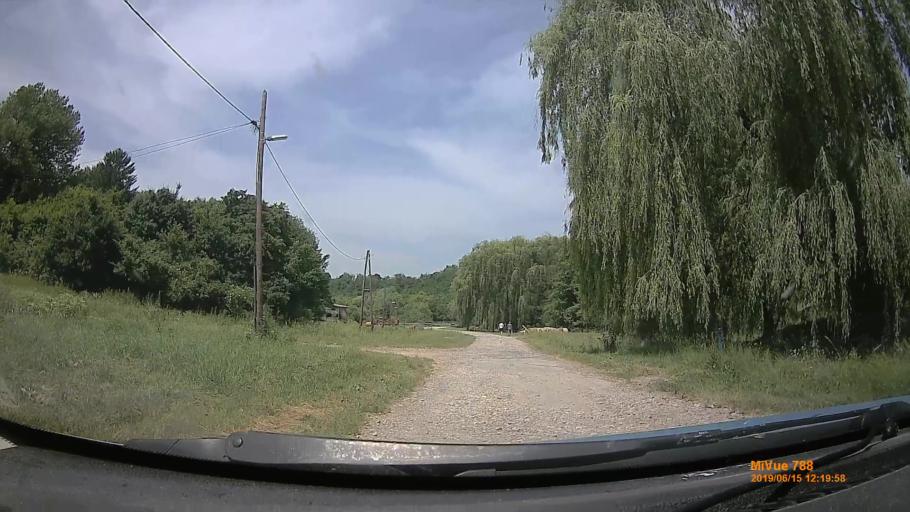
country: HU
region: Baranya
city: Buekkoesd
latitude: 46.1061
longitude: 18.0160
